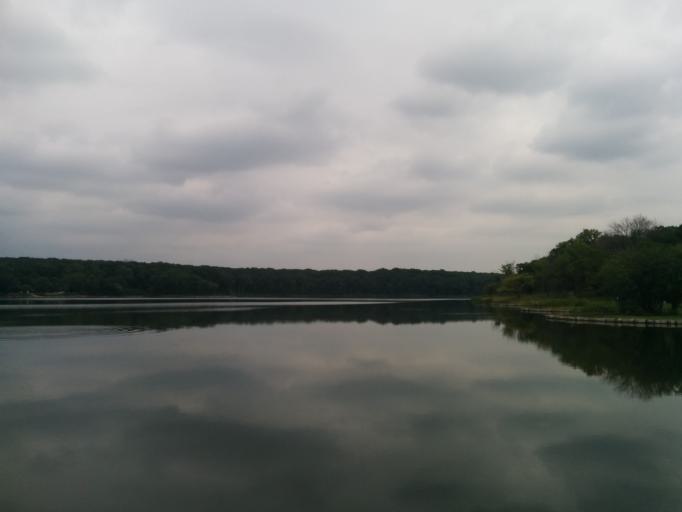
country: US
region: Illinois
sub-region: DuPage County
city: Burr Ridge
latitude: 41.7125
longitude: -87.8942
